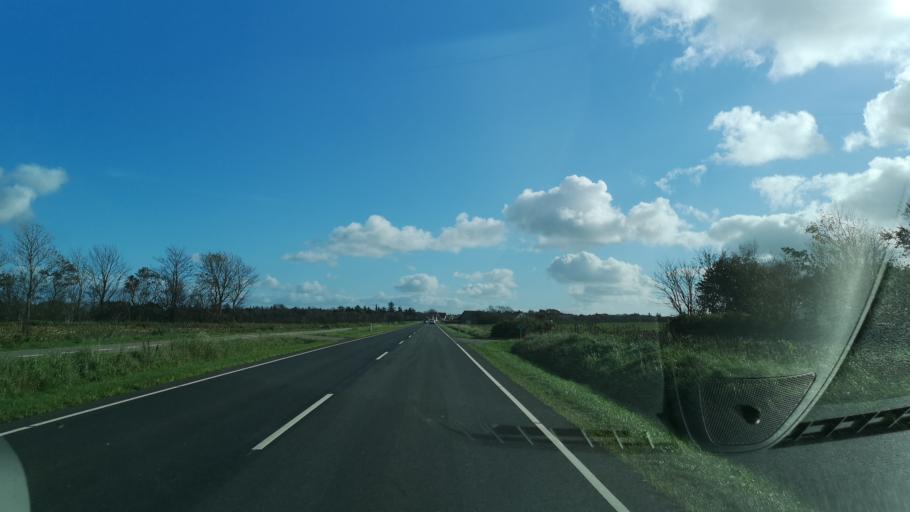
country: DK
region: South Denmark
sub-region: Varde Kommune
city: Oksbol
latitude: 55.7178
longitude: 8.2939
